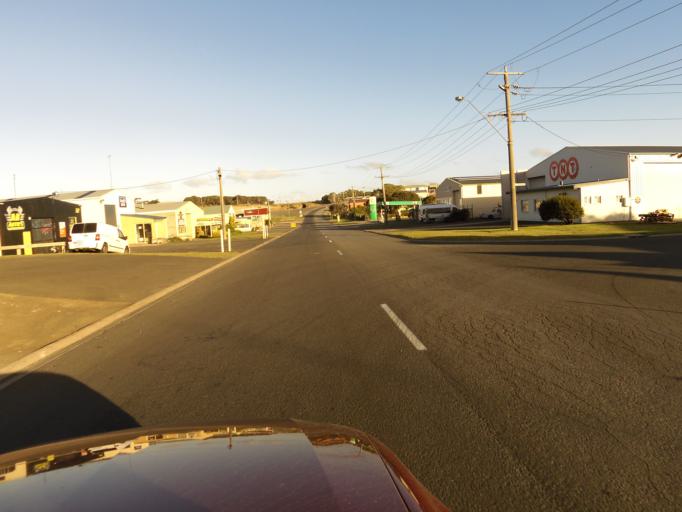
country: AU
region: Victoria
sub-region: Warrnambool
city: Warrnambool
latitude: -38.3705
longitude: 142.4590
